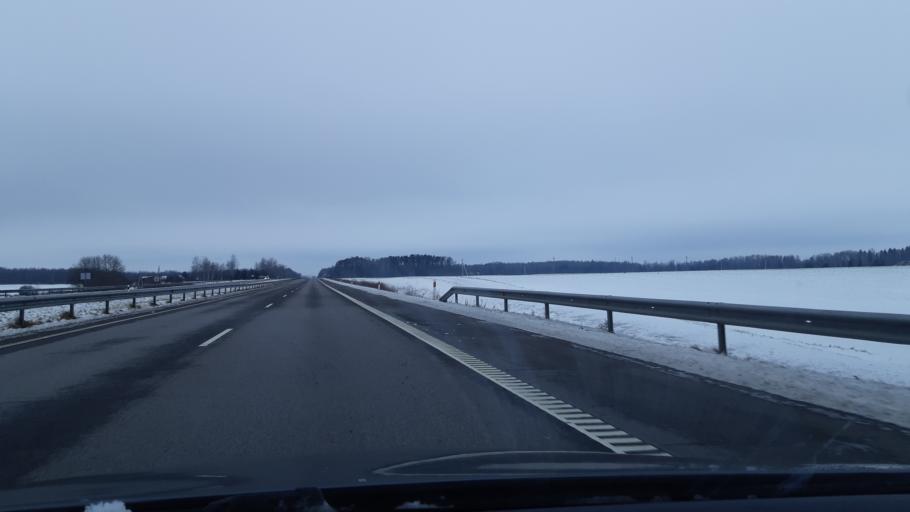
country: LT
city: Vilkija
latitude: 55.1209
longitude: 23.7559
